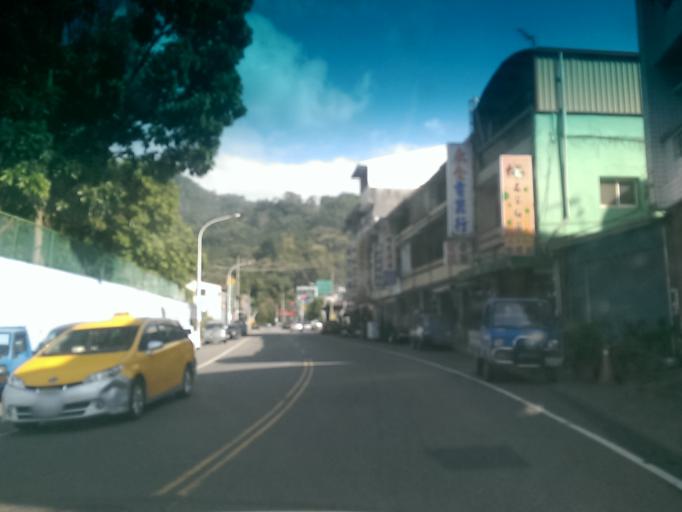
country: TW
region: Taiwan
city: Lugu
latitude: 23.8085
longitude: 120.8582
